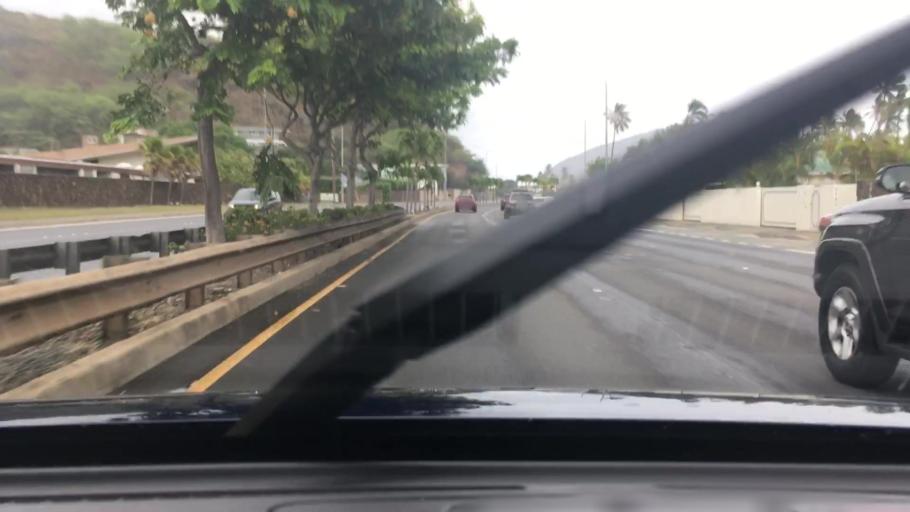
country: US
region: Hawaii
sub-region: Honolulu County
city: Waimanalo Beach
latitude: 21.2822
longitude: -157.7338
